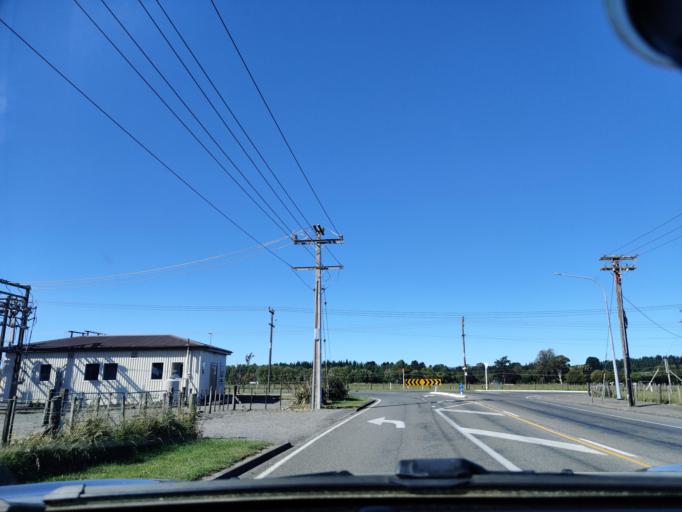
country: NZ
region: Wellington
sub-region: Masterton District
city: Masterton
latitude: -40.9367
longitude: 175.6516
